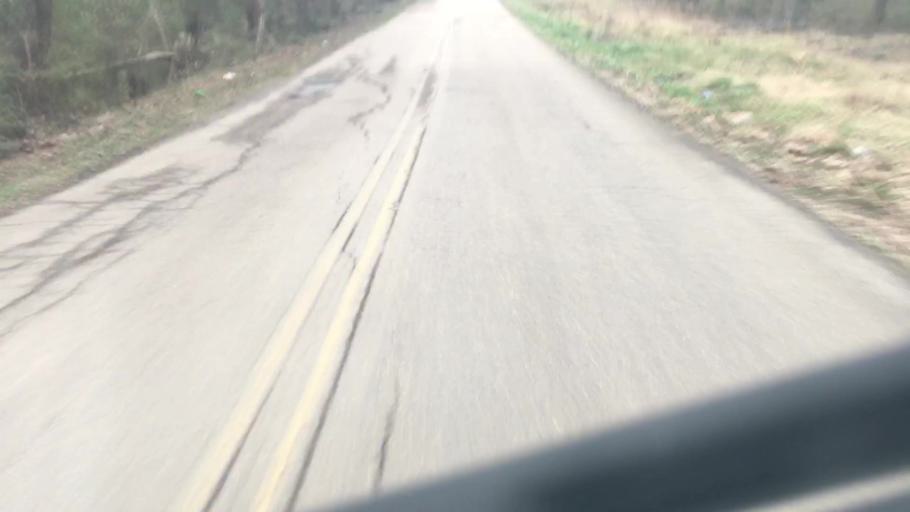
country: US
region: Alabama
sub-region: Walker County
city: Jasper
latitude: 33.8317
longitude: -87.2253
